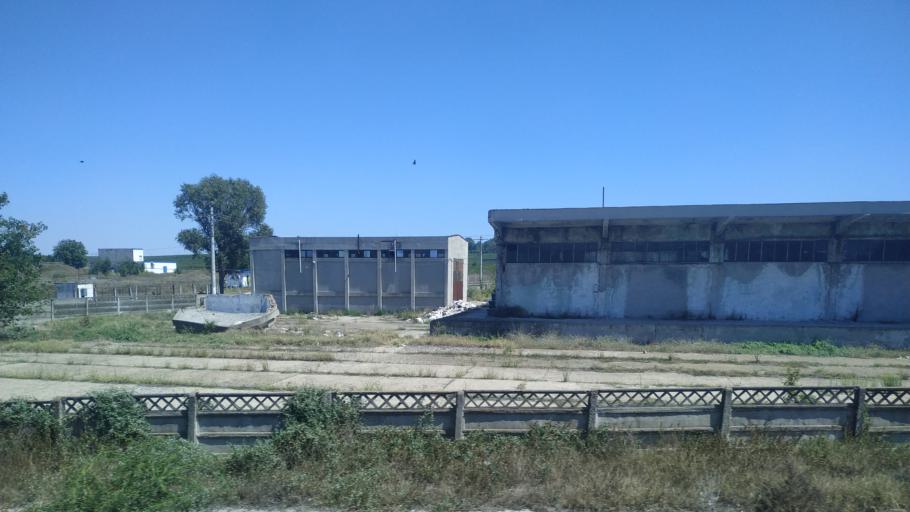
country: RO
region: Constanta
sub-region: Oras Murfatlar
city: Murfatlar
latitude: 44.1805
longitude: 28.3991
